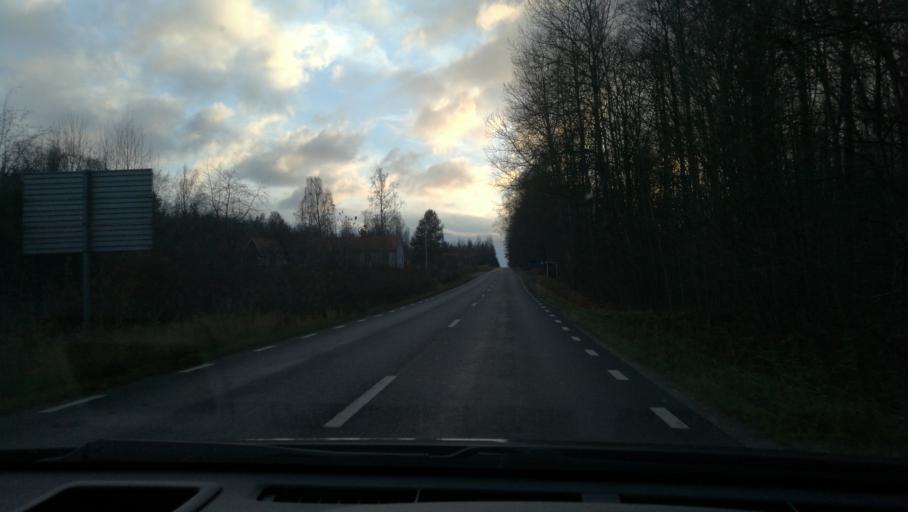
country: SE
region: Soedermanland
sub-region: Vingakers Kommun
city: Vingaker
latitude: 59.1614
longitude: 15.9360
